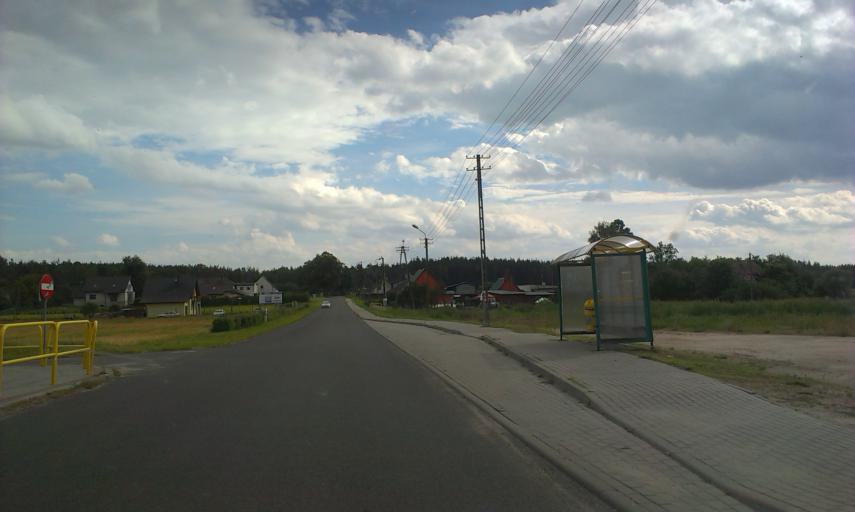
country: PL
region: Greater Poland Voivodeship
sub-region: Powiat zlotowski
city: Zlotow
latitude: 53.4437
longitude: 16.9851
